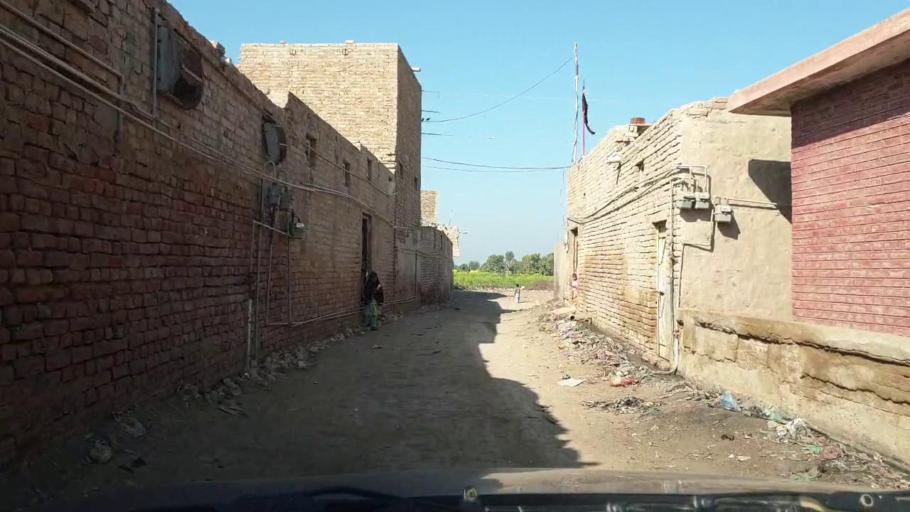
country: PK
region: Sindh
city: Jhol
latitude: 25.9434
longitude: 68.8196
